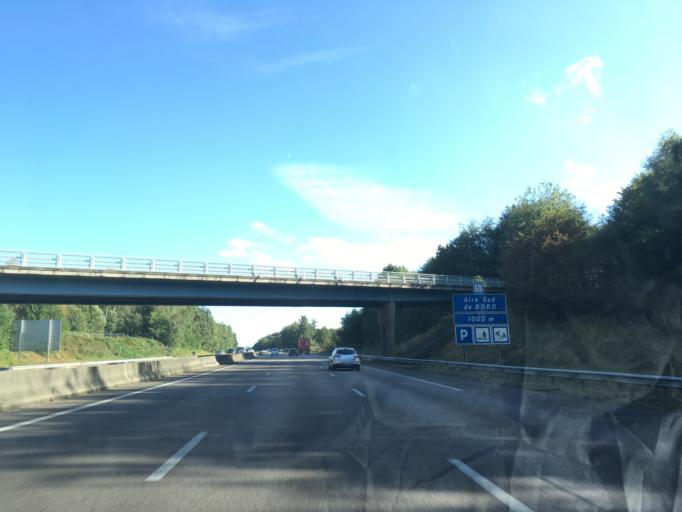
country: FR
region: Haute-Normandie
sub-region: Departement de l'Eure
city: Criquebeuf-sur-Seine
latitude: 49.2776
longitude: 1.1295
